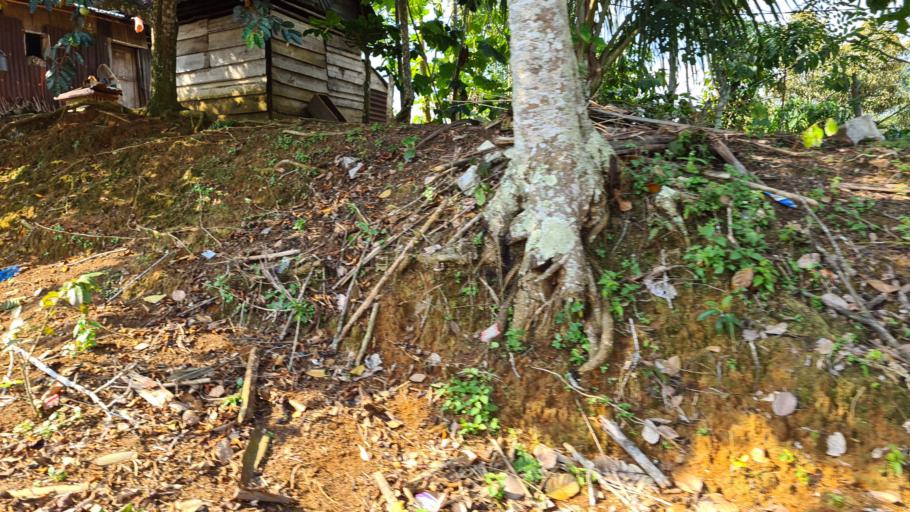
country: ID
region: Lampung
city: Kuripan
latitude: -5.0694
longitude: 103.8707
